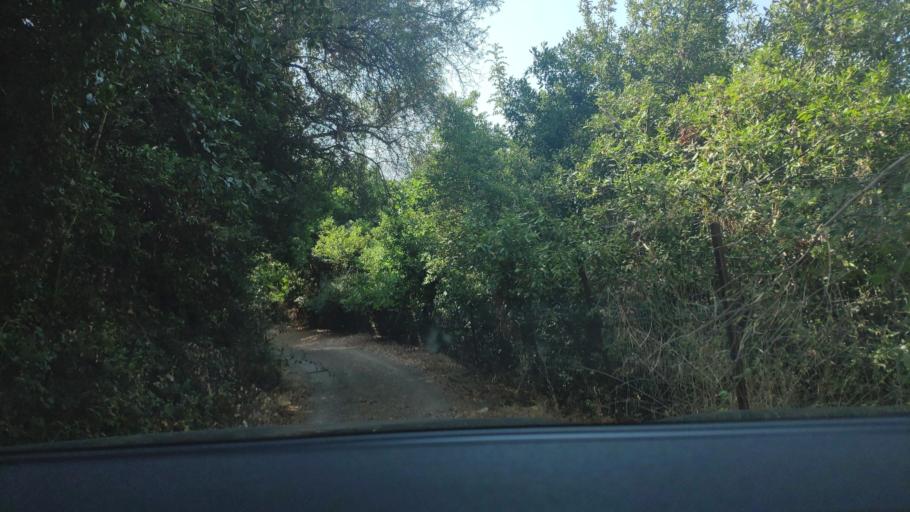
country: GR
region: West Greece
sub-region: Nomos Aitolias kai Akarnanias
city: Fitiai
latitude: 38.7253
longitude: 21.1894
